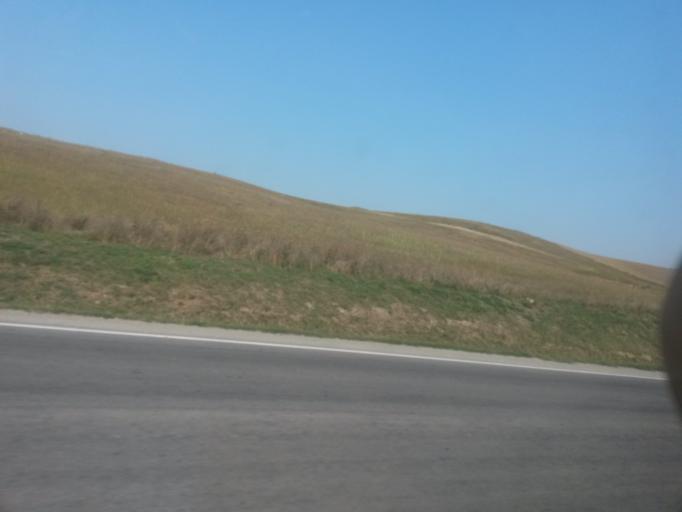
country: RO
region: Cluj
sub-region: Comuna Sandulesti
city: Copaceni
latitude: 46.5890
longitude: 23.7556
